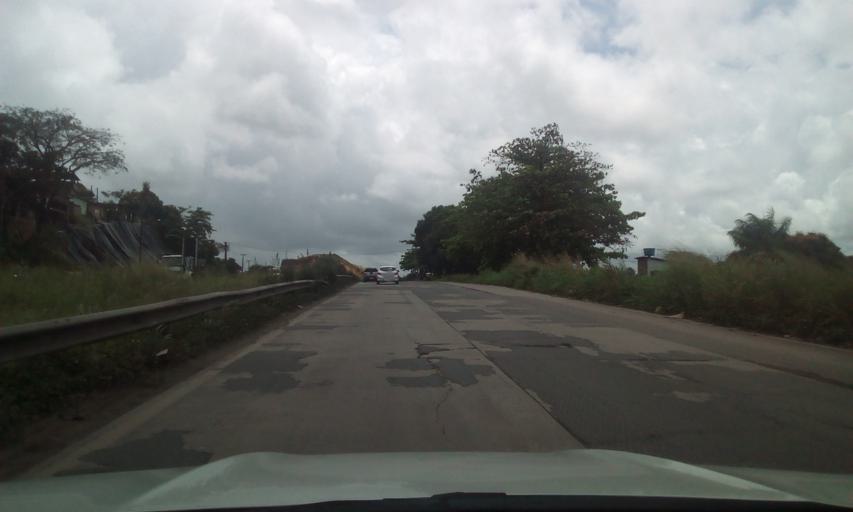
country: BR
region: Pernambuco
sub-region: Jaboatao Dos Guararapes
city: Jaboatao dos Guararapes
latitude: -8.1110
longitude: -34.9461
